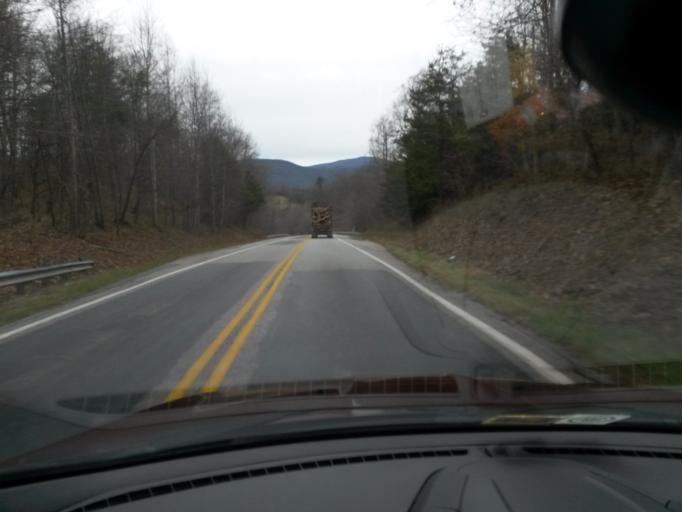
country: US
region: Virginia
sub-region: Amherst County
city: Amherst
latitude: 37.6557
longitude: -79.1395
